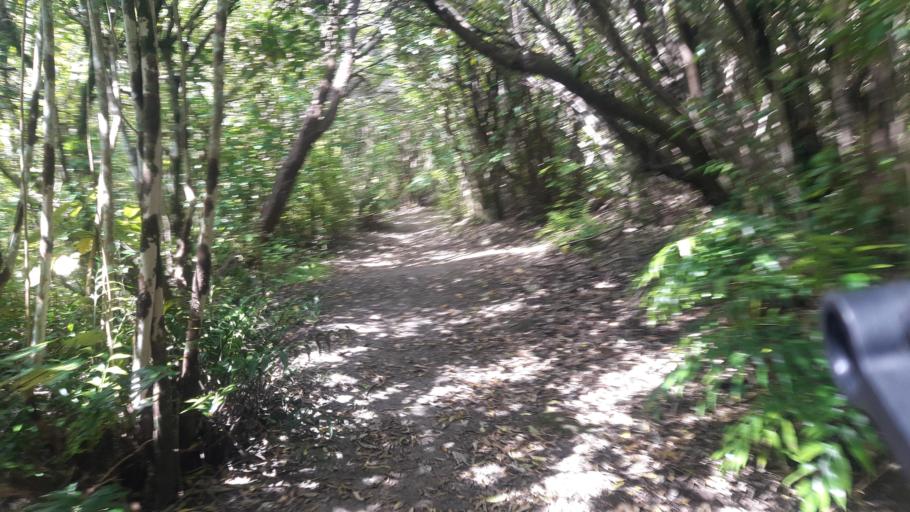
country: NZ
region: Marlborough
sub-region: Marlborough District
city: Picton
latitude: -41.2557
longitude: 174.0392
